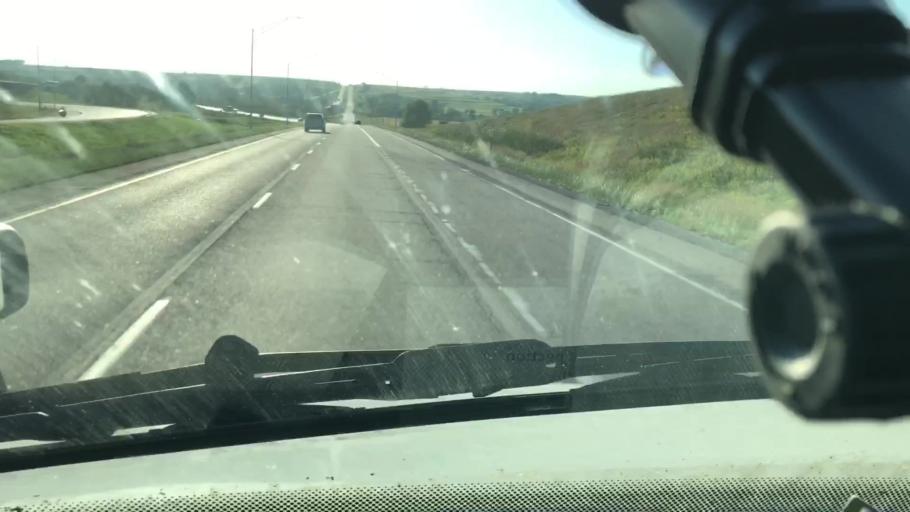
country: US
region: Iowa
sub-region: Pottawattamie County
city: Avoca
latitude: 41.4990
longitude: -95.5756
